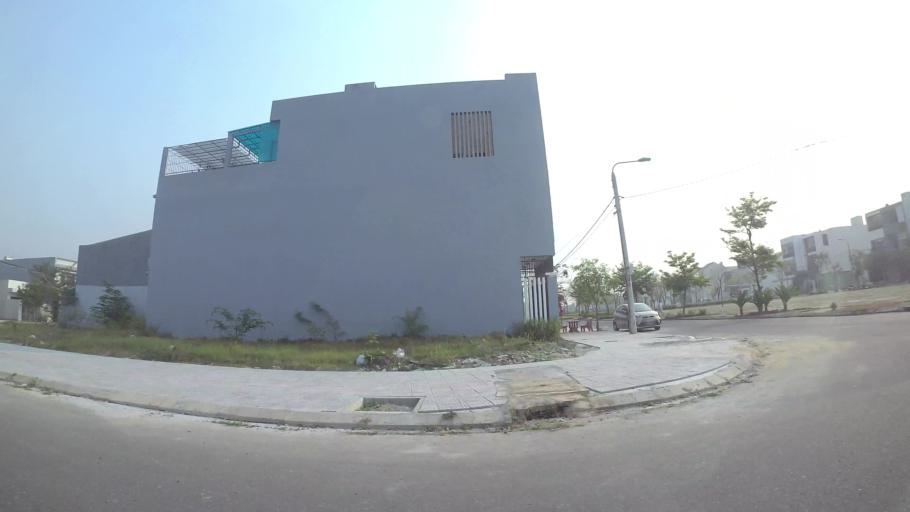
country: VN
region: Da Nang
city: Cam Le
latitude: 16.0144
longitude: 108.2185
